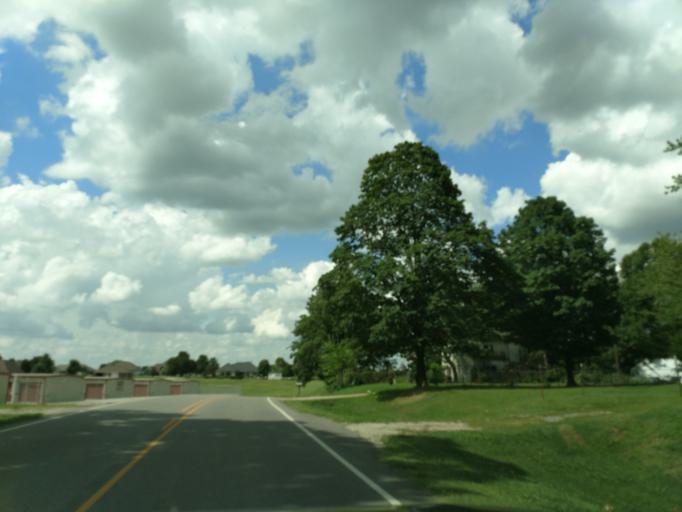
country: US
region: Arkansas
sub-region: Carroll County
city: Berryville
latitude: 36.3829
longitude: -93.5672
